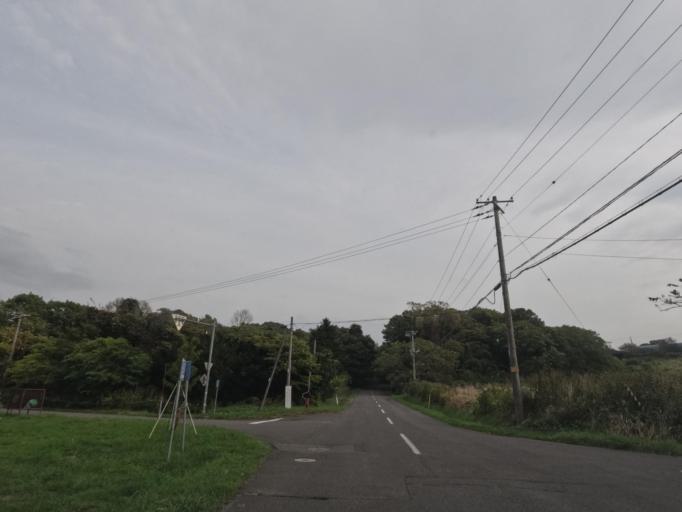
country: JP
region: Hokkaido
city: Date
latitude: 42.4120
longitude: 140.9146
